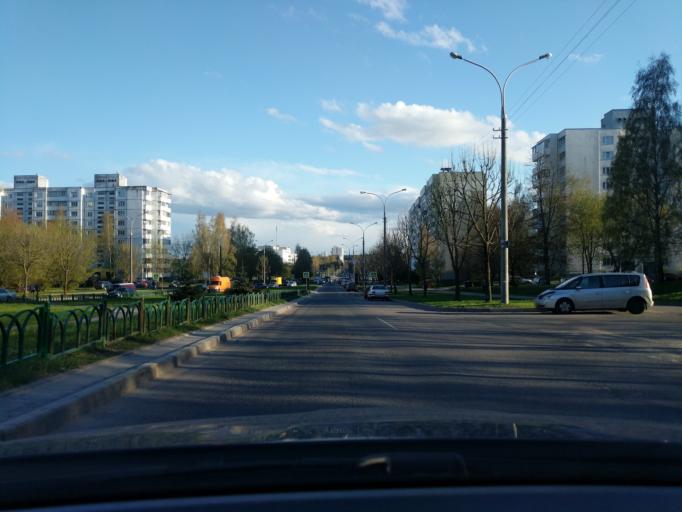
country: BY
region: Minsk
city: Novoye Medvezhino
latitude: 53.9023
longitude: 27.4529
